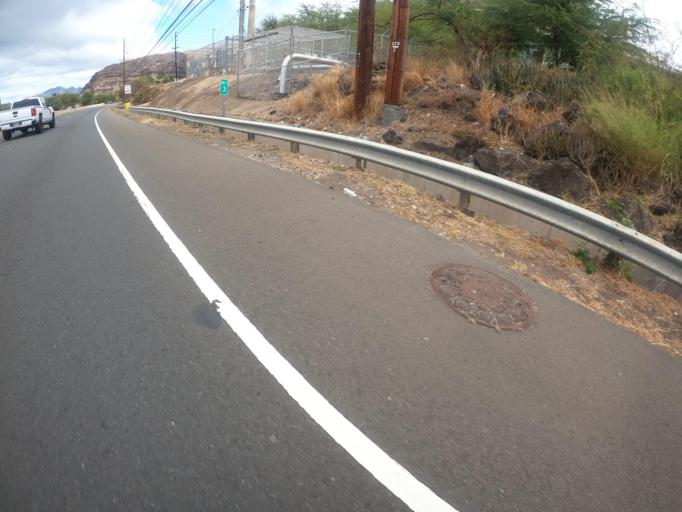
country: US
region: Hawaii
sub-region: Honolulu County
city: Makakilo
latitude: 21.3509
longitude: -158.1292
